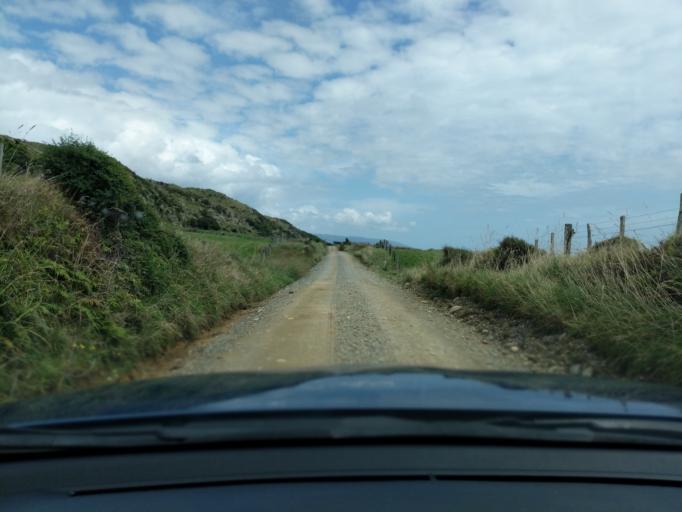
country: NZ
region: Tasman
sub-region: Tasman District
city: Takaka
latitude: -40.6643
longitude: 172.4091
